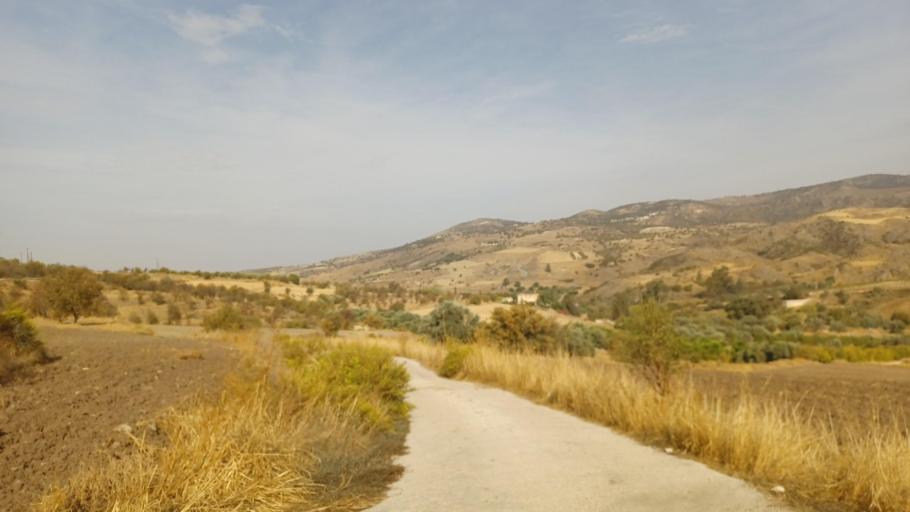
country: CY
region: Pafos
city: Polis
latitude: 34.9497
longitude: 32.5152
